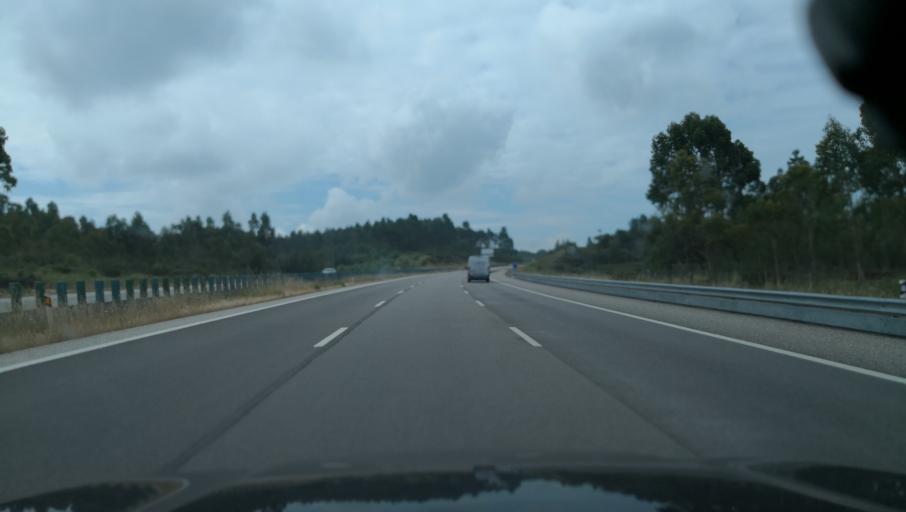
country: PT
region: Leiria
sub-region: Leiria
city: Souto da Carpalhosa
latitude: 39.8612
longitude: -8.8247
